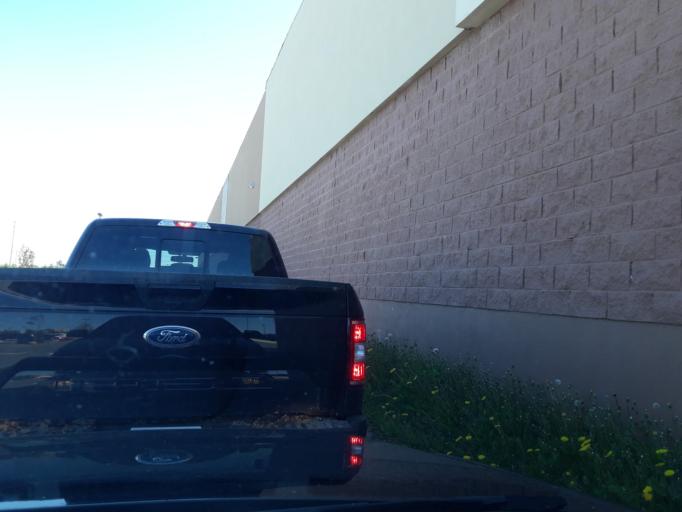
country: CA
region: Newfoundland and Labrador
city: St. John's
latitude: 47.6142
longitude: -52.7157
